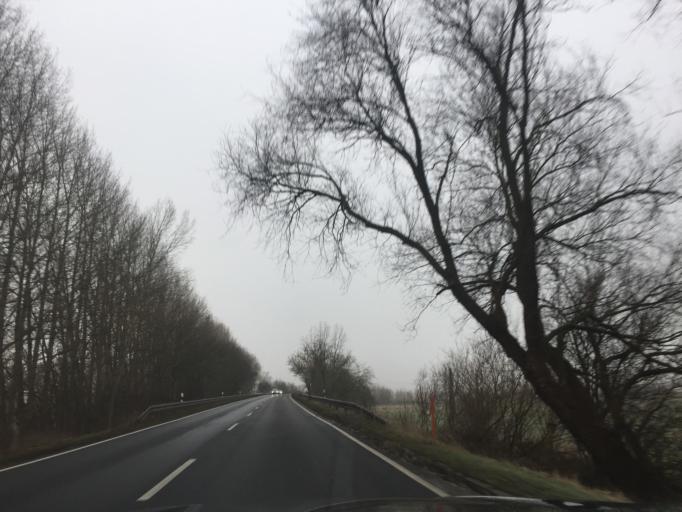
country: DE
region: Brandenburg
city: Velten
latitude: 52.6447
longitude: 13.1472
